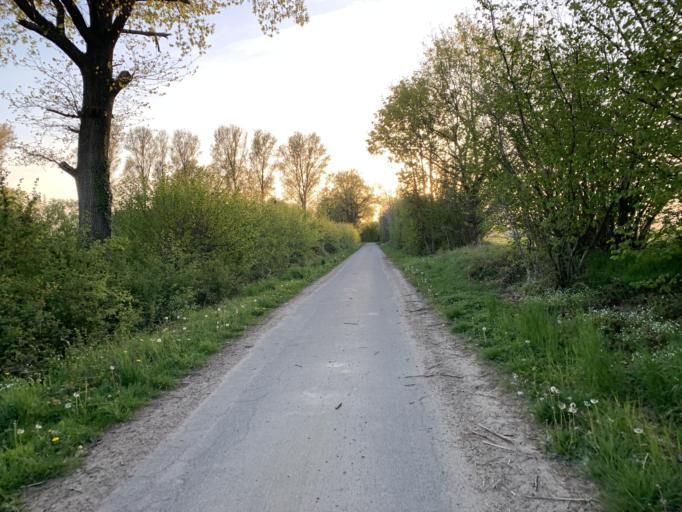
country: DE
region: Schleswig-Holstein
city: Worth
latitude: 53.4687
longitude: 10.4199
